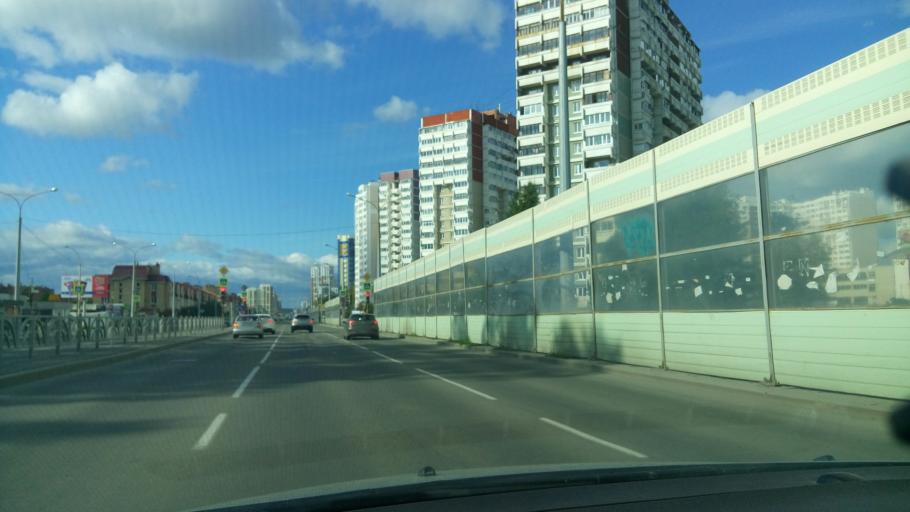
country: RU
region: Sverdlovsk
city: Sovkhoznyy
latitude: 56.7805
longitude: 60.5444
